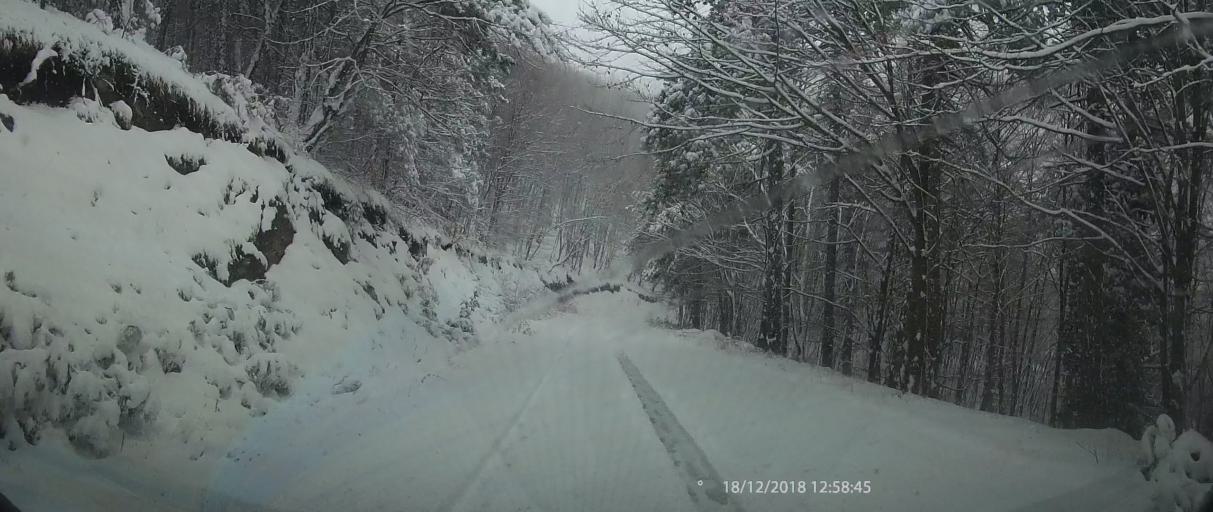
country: GR
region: Central Macedonia
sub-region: Nomos Pierias
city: Litochoro
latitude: 40.1072
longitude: 22.4623
